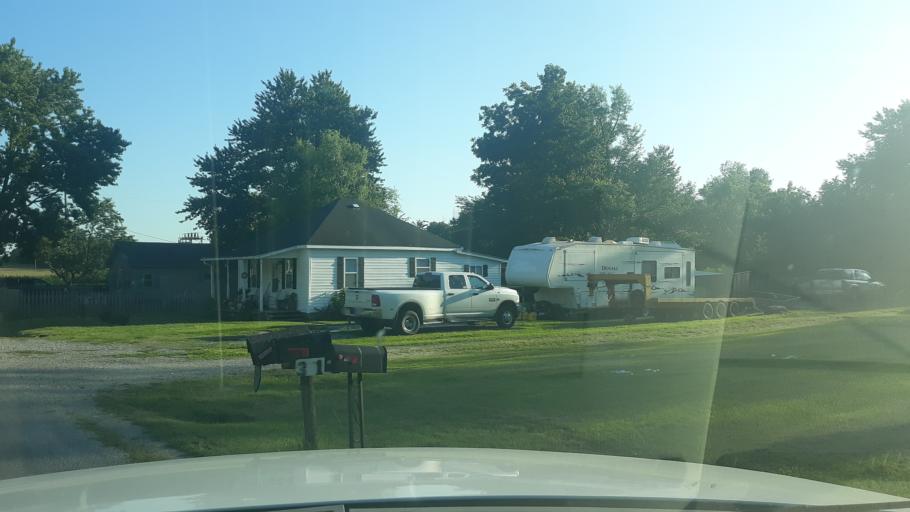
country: US
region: Illinois
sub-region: Saline County
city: Harrisburg
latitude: 37.8378
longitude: -88.6132
